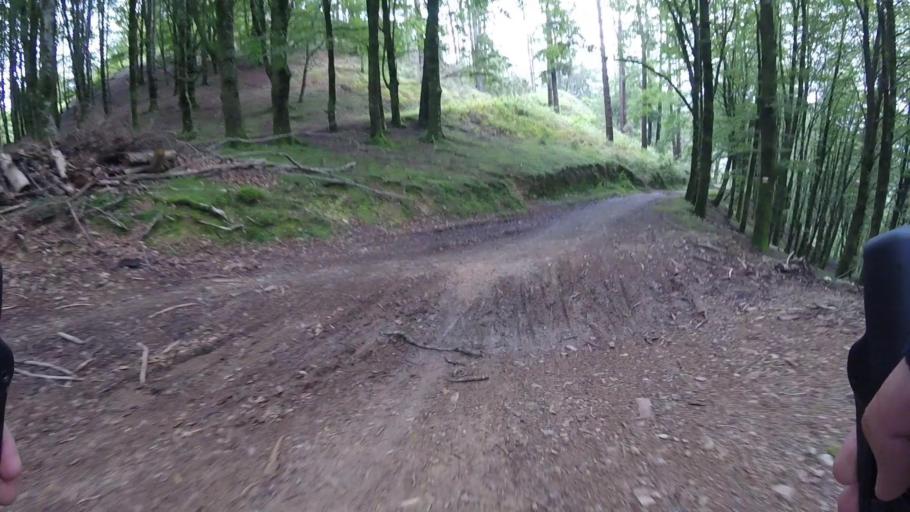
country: ES
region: Navarre
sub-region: Provincia de Navarra
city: Arano
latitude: 43.2534
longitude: -1.8703
